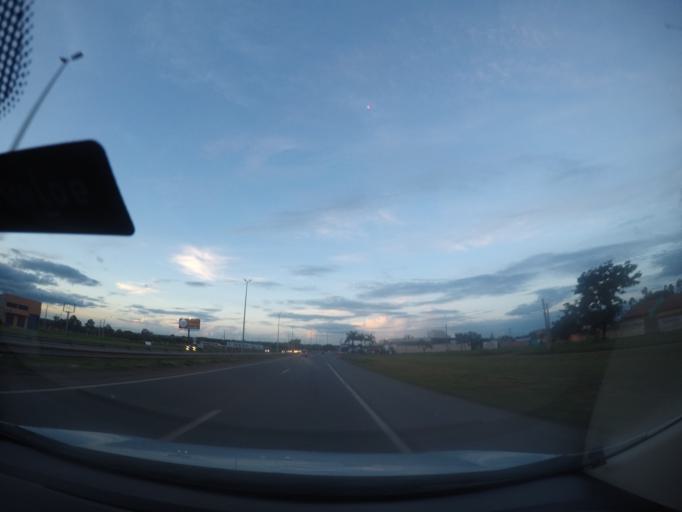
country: BR
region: Goias
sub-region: Goianira
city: Goianira
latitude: -16.5493
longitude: -49.4055
